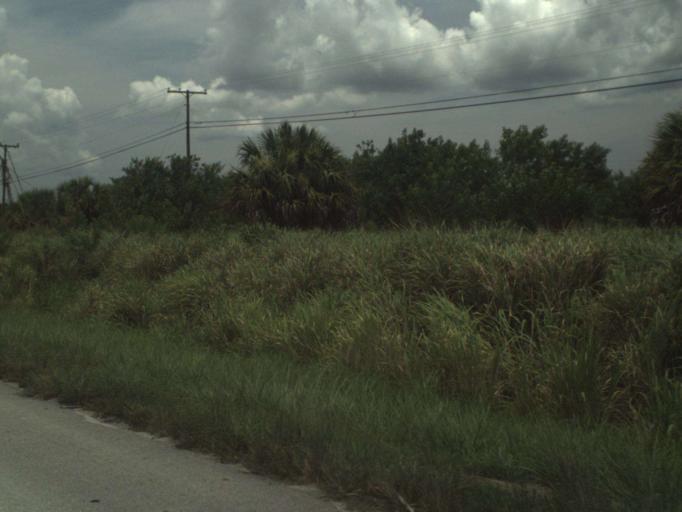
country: US
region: Florida
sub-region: Saint Lucie County
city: Lakewood Park
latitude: 27.5022
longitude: -80.3985
